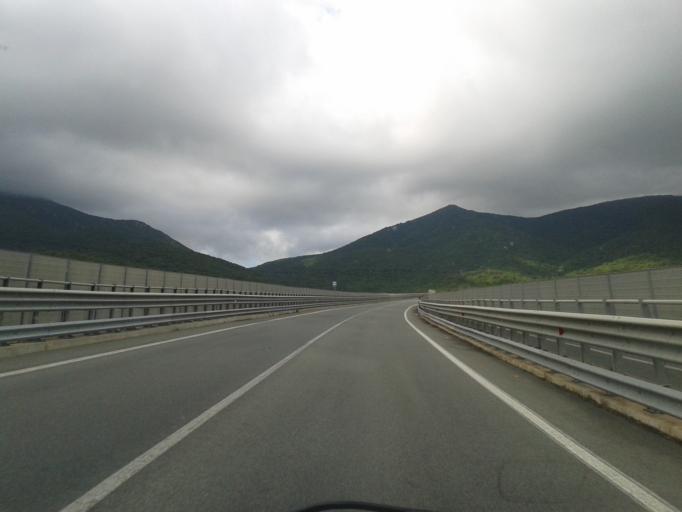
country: IT
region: Sardinia
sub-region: Provincia di Cagliari
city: Castiadas
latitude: 39.2286
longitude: 9.5030
